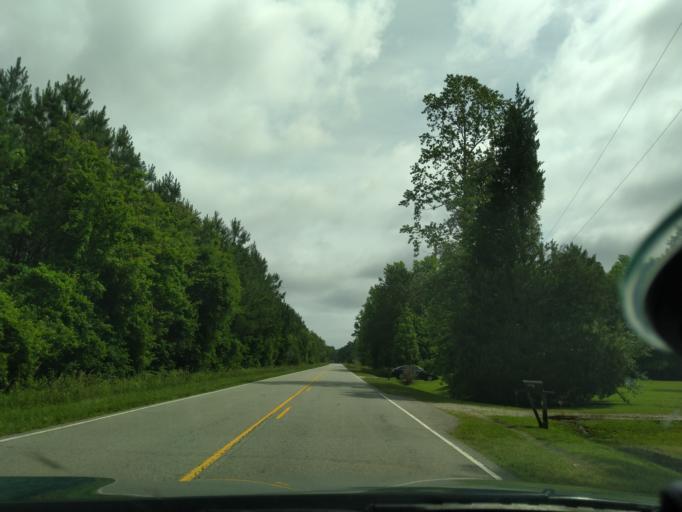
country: US
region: North Carolina
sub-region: Chowan County
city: Edenton
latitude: 35.9213
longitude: -76.5961
